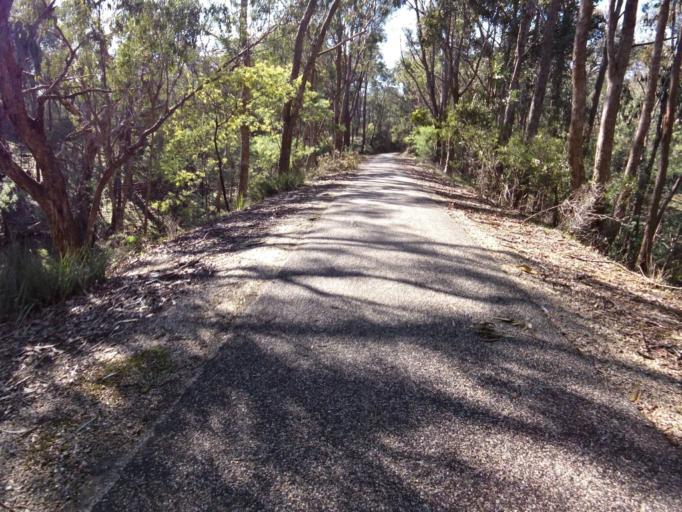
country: AU
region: Victoria
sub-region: Wangaratta
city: Wangaratta
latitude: -36.4034
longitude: 146.6346
